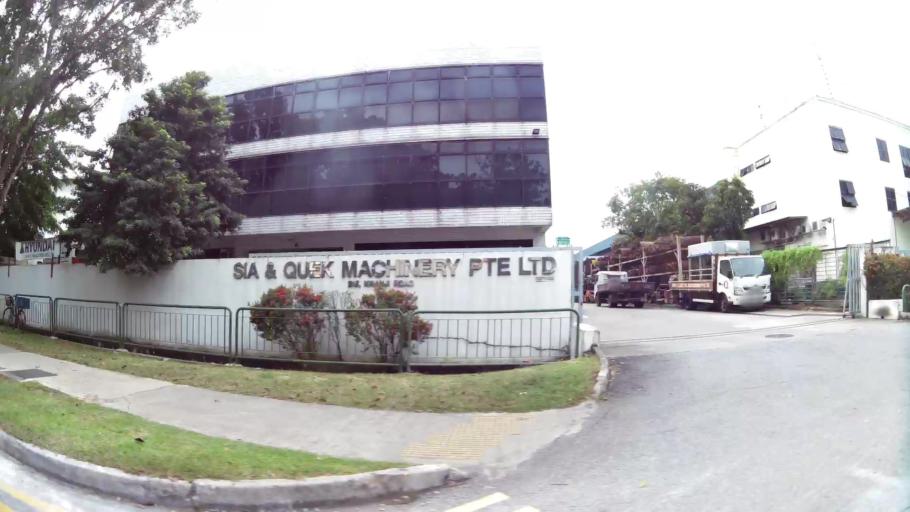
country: MY
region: Johor
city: Johor Bahru
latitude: 1.4355
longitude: 103.7549
